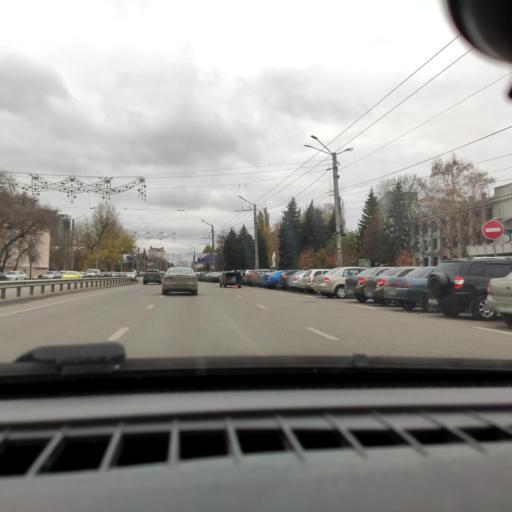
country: RU
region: Voronezj
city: Voronezh
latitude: 51.6537
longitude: 39.1697
